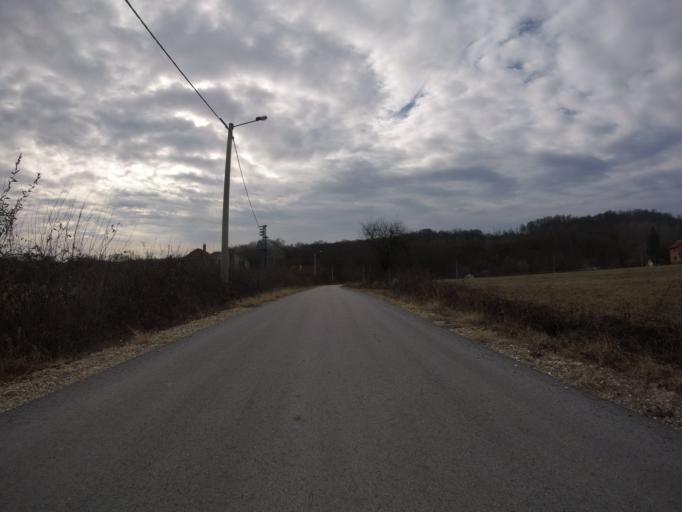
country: HR
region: Sisacko-Moslavacka
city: Glina
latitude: 45.4390
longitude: 16.0747
